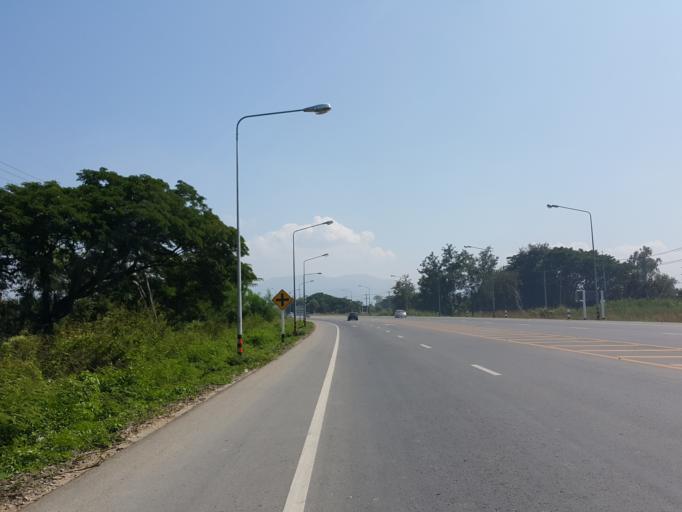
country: TH
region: Chiang Mai
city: San Kamphaeng
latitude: 18.7131
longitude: 99.1227
